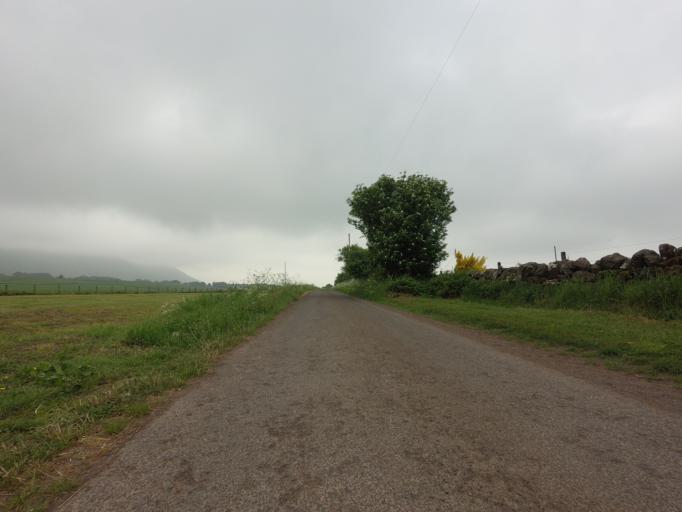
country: GB
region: Scotland
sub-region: Fife
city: Ballingry
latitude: 56.2374
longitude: -3.3441
